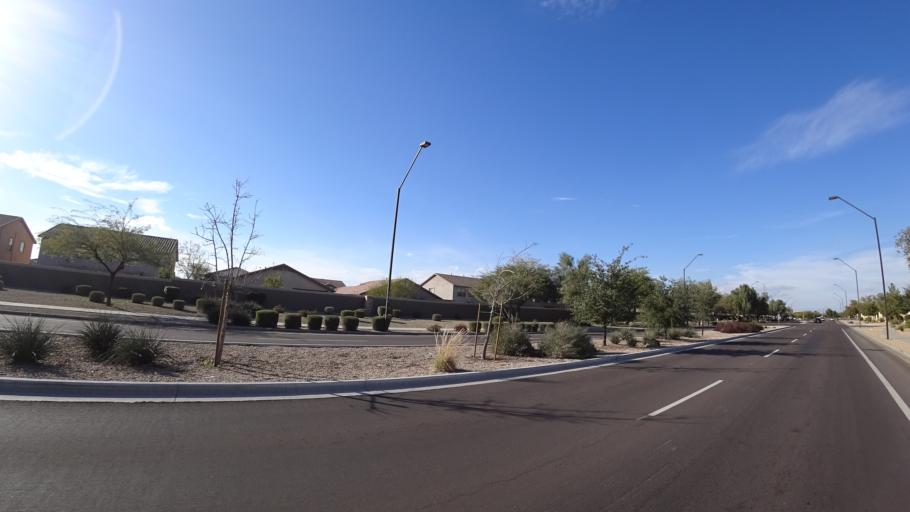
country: US
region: Arizona
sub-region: Maricopa County
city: Peoria
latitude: 33.5709
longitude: -112.2376
